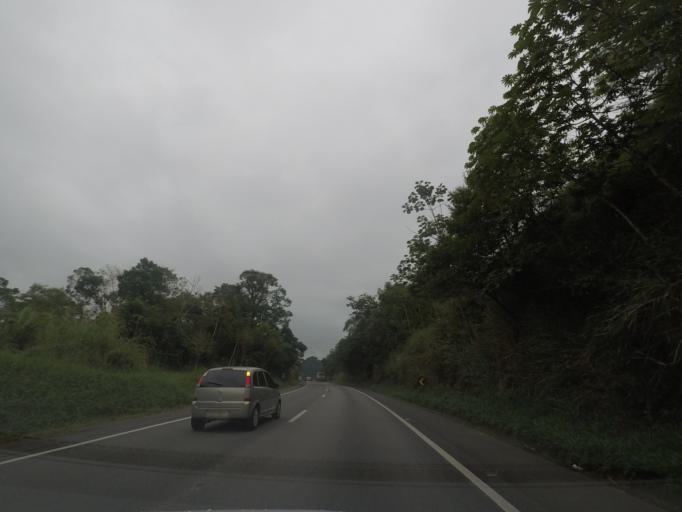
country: BR
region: Sao Paulo
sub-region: Cajati
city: Cajati
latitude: -24.7851
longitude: -48.2033
